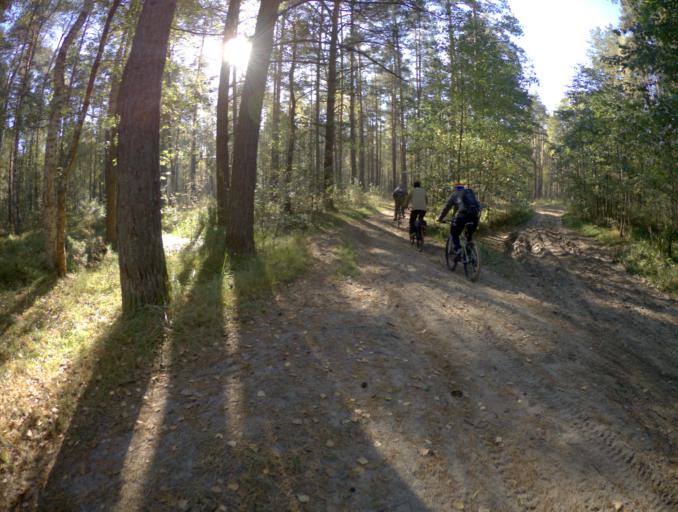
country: RU
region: Vladimir
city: Sobinka
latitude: 55.9748
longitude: 40.0070
